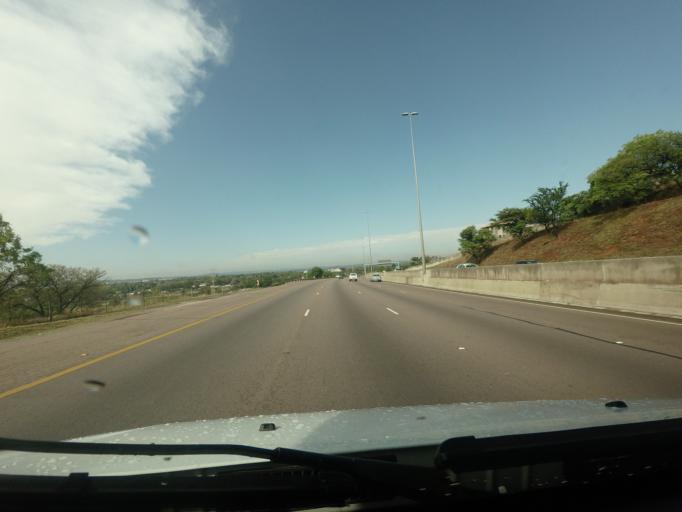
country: ZA
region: Gauteng
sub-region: City of Tshwane Metropolitan Municipality
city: Pretoria
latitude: -25.6981
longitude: 28.2803
